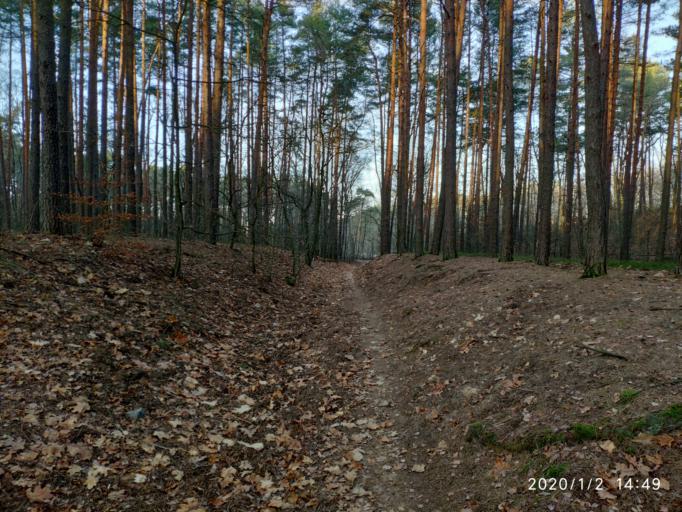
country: PL
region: Lubusz
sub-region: Zielona Gora
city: Zielona Gora
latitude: 51.9238
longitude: 15.4764
